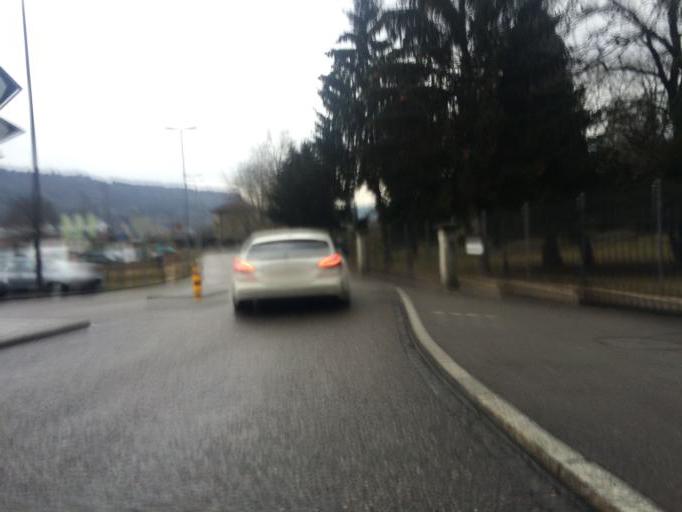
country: CH
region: Aargau
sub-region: Bezirk Brugg
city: Brugg
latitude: 47.4817
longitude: 8.2128
